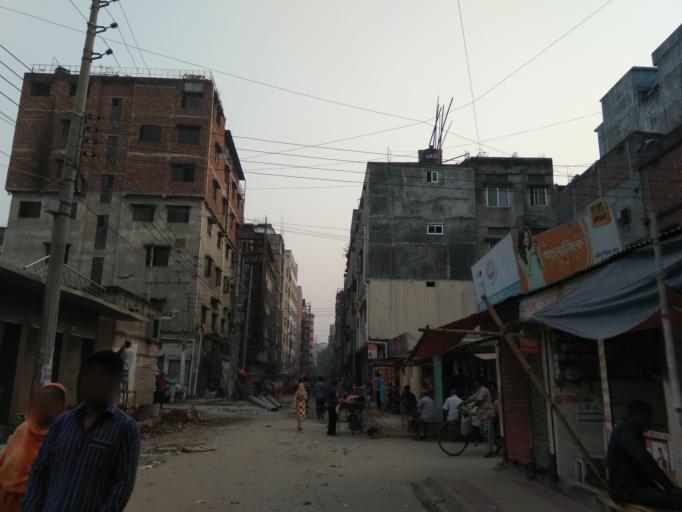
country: BD
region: Dhaka
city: Tungi
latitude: 23.8185
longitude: 90.3637
